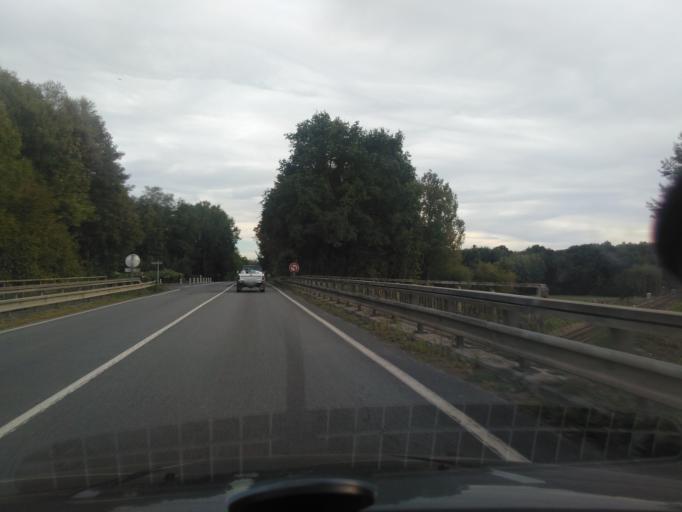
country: FR
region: Picardie
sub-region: Departement de l'Aisne
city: Laon
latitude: 49.5646
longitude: 3.5913
